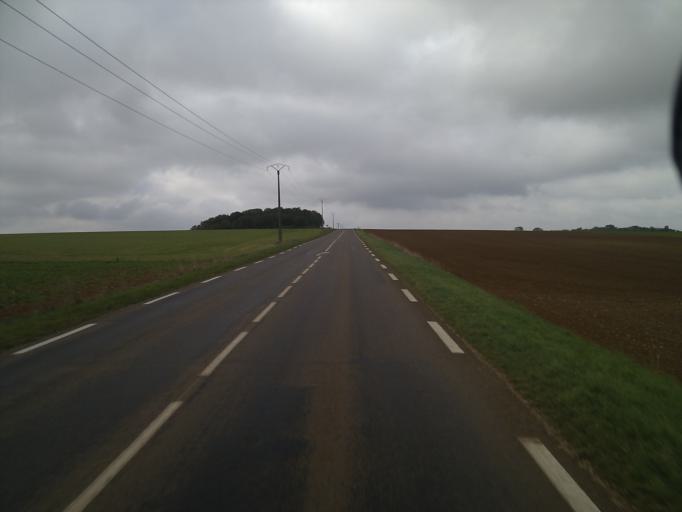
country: FR
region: Champagne-Ardenne
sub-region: Departement de la Haute-Marne
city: Doulaincourt-Saucourt
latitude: 48.2174
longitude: 5.2803
